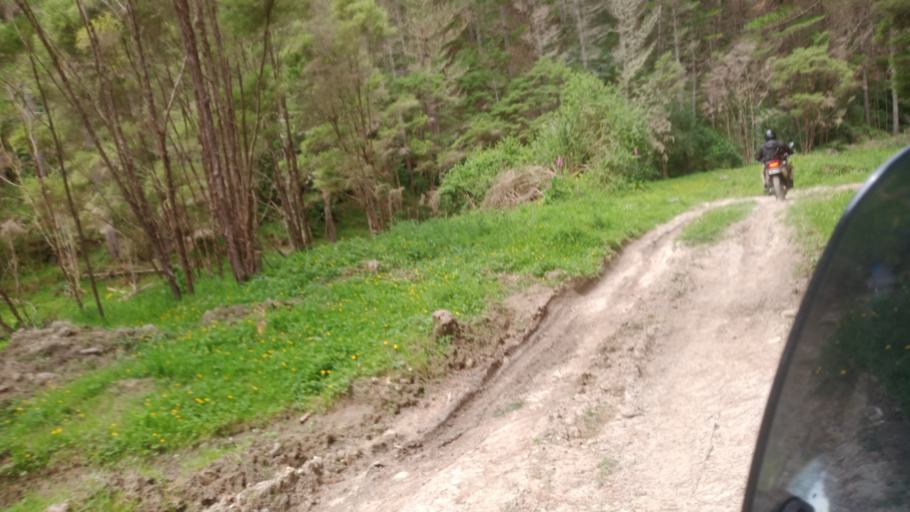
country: NZ
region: Gisborne
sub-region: Gisborne District
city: Gisborne
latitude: -38.4570
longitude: 177.9291
